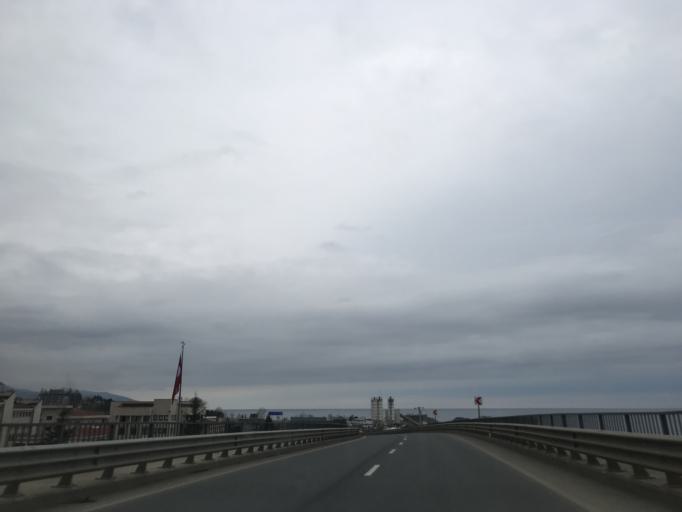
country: TR
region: Trabzon
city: Akcaabat
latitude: 41.0027
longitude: 39.6357
